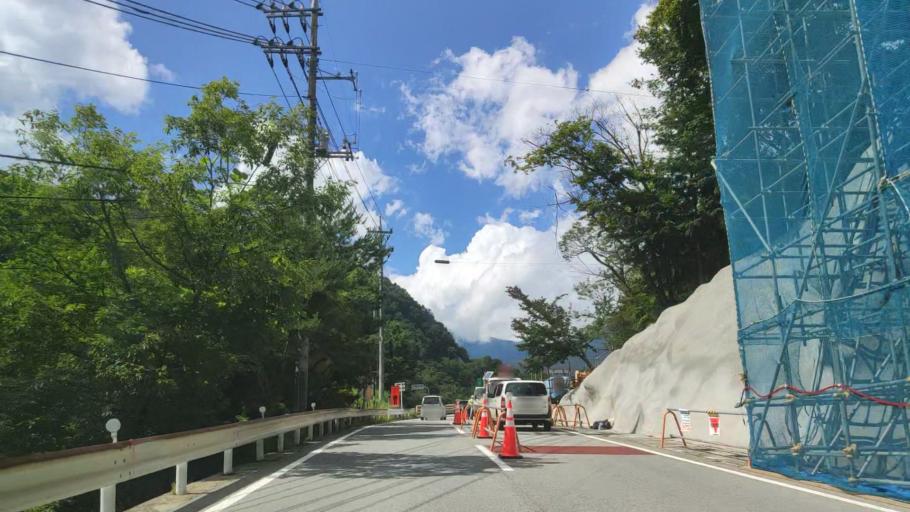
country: JP
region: Yamanashi
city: Enzan
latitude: 35.8312
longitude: 138.7643
